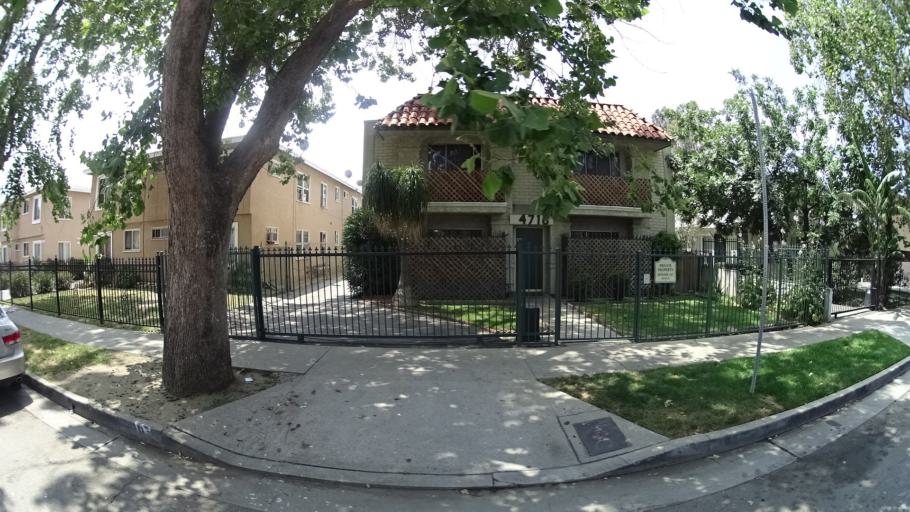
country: US
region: California
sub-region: Los Angeles County
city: Van Nuys
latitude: 34.1876
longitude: -118.4538
